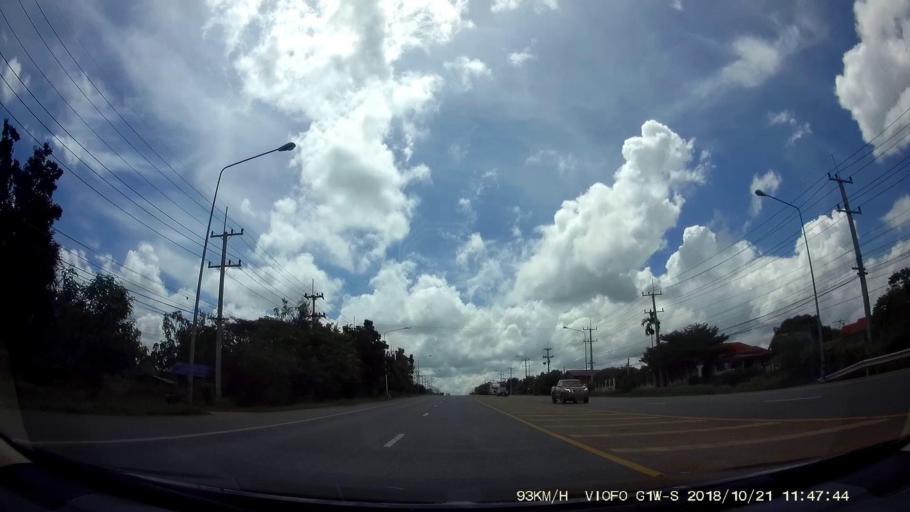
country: TH
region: Chaiyaphum
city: Noen Sa-nga
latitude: 15.6574
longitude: 101.9521
